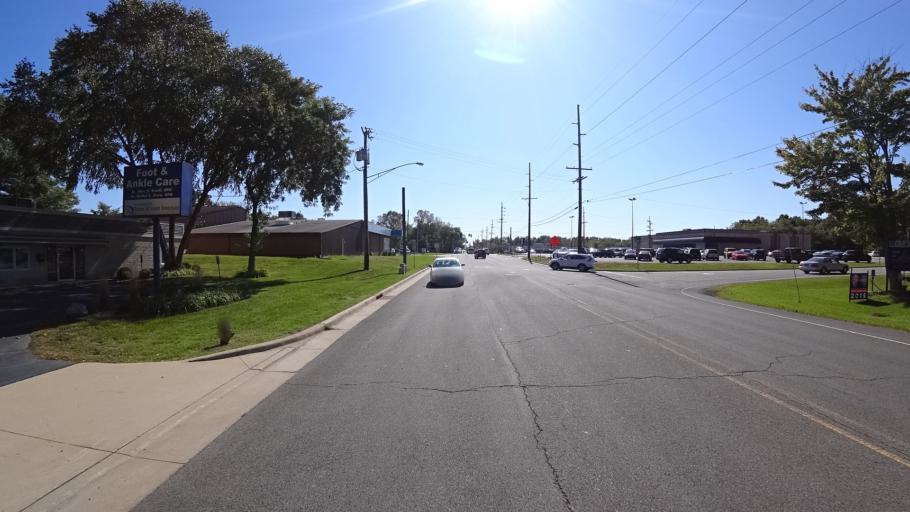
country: US
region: Indiana
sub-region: LaPorte County
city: Trail Creek
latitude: 41.6885
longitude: -86.8744
